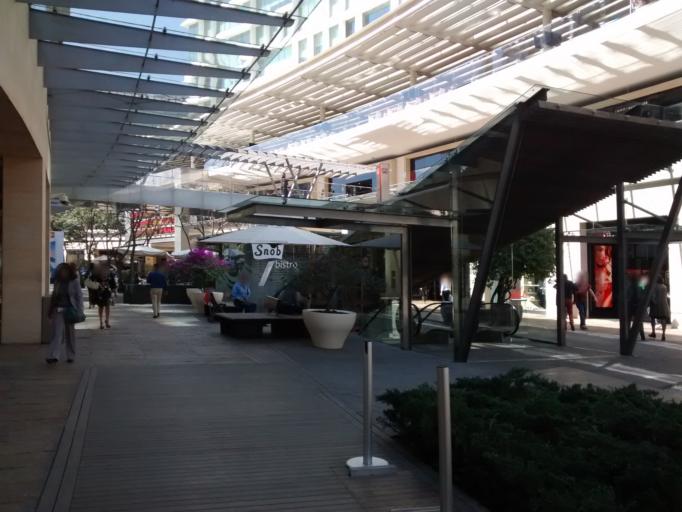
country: MX
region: Mexico City
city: Miguel Hidalgo
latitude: 19.4393
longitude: -99.2020
